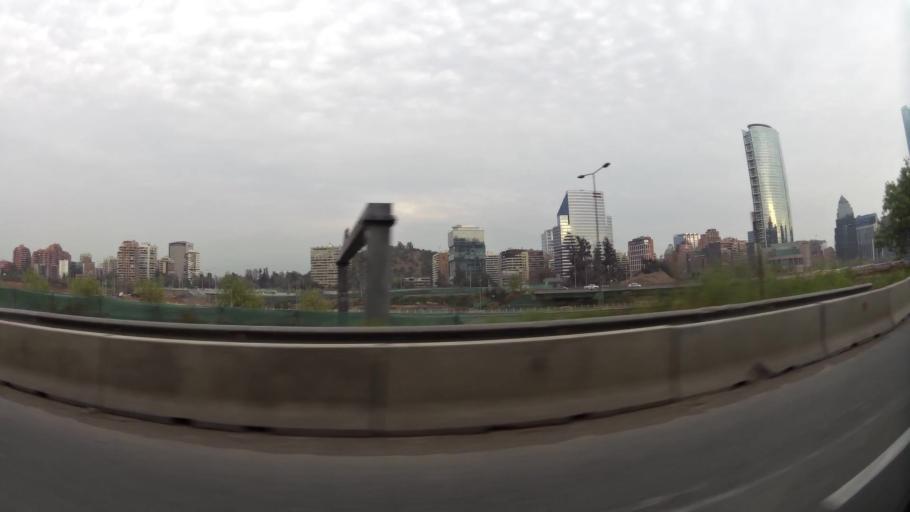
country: CL
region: Santiago Metropolitan
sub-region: Provincia de Santiago
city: Villa Presidente Frei, Nunoa, Santiago, Chile
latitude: -33.4081
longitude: -70.6059
